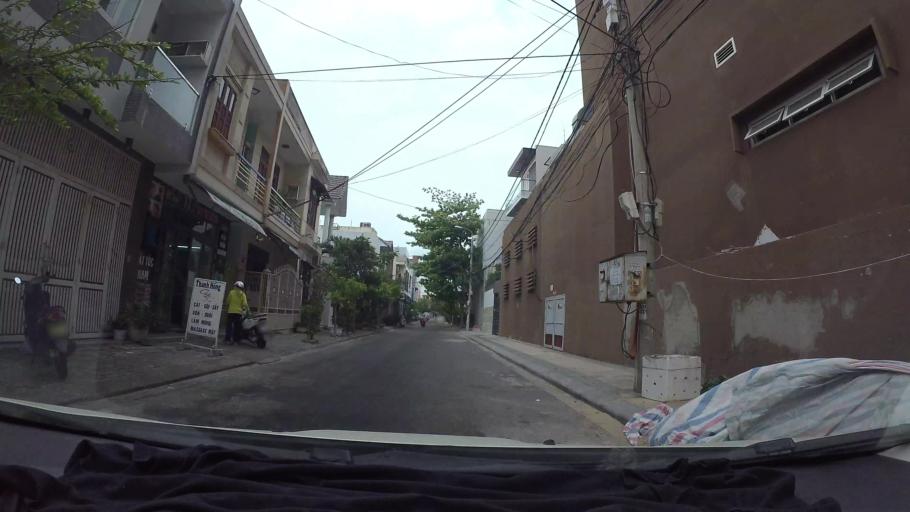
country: VN
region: Da Nang
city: Da Nang
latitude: 16.0857
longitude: 108.2179
